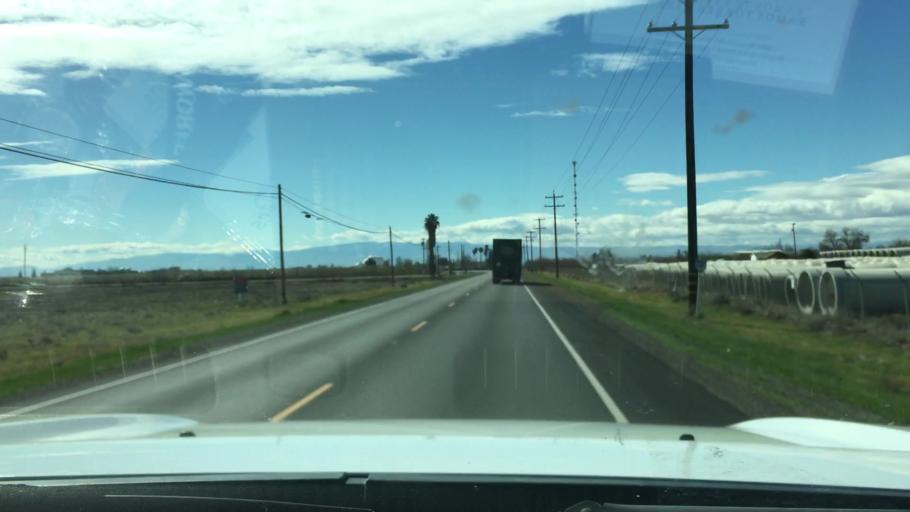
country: US
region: California
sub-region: Kern County
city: Shafter
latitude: 35.4621
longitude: -119.2610
